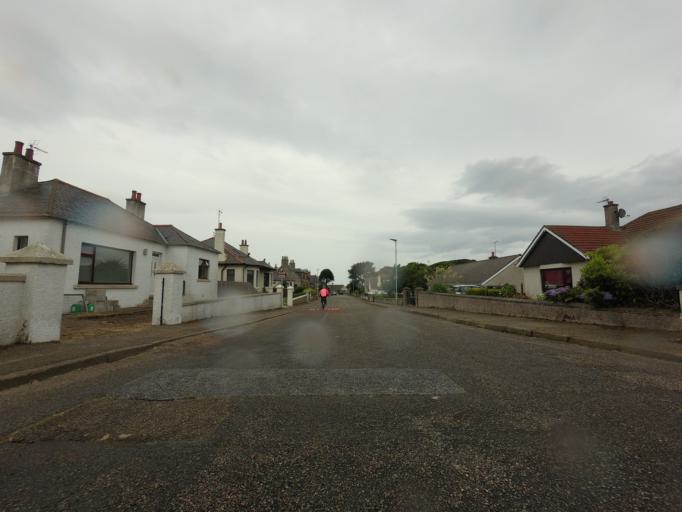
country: GB
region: Scotland
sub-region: Moray
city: Cullen
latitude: 57.6875
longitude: -2.8182
